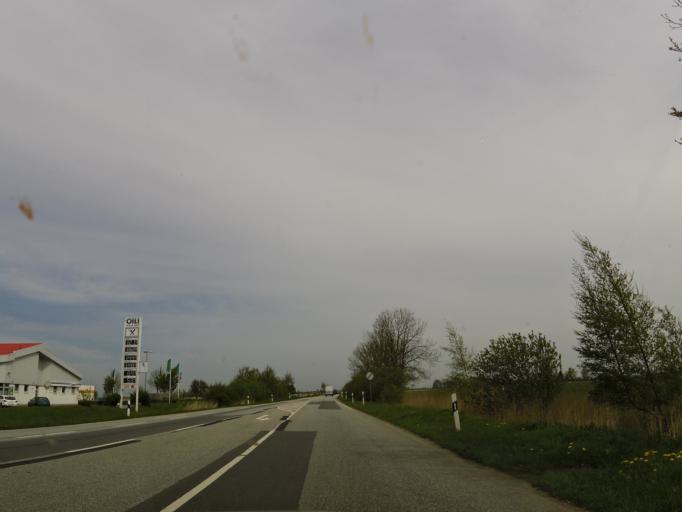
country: DE
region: Schleswig-Holstein
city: Koldenbuttel
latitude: 54.4132
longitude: 9.0434
